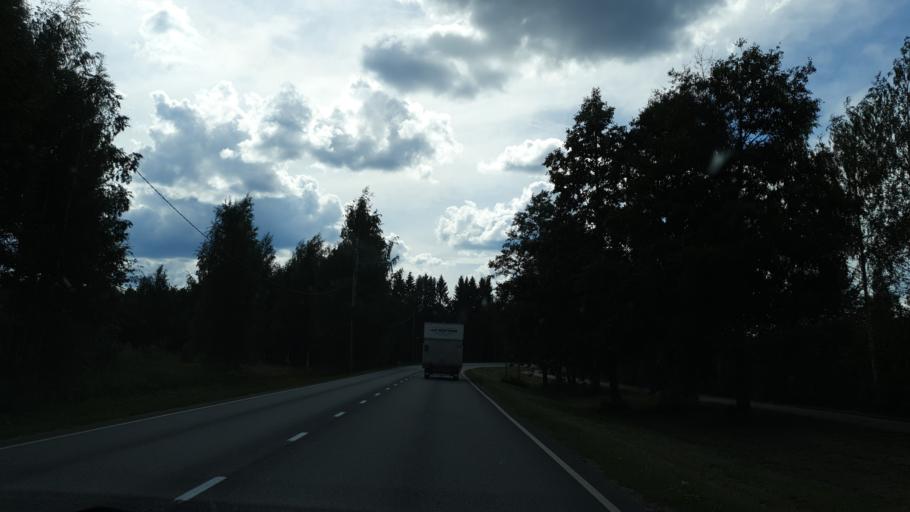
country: FI
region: Kainuu
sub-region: Kajaani
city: Sotkamo
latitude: 64.1351
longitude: 28.4093
